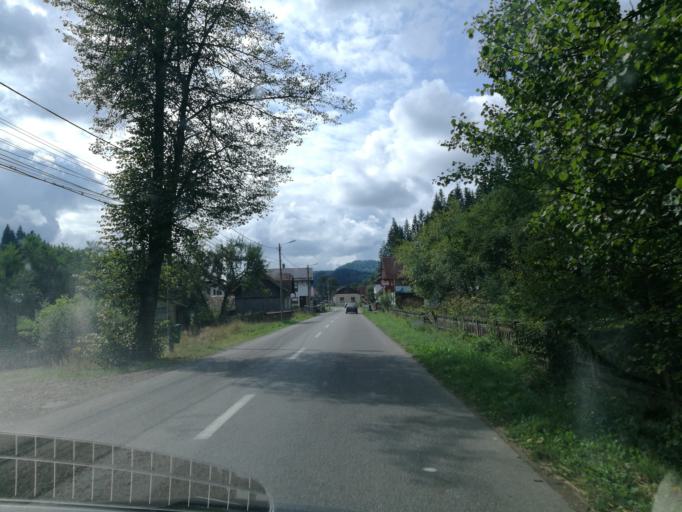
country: RO
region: Suceava
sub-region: Oras Gura Humorului
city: Gura Humorului
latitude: 47.5296
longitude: 25.8637
